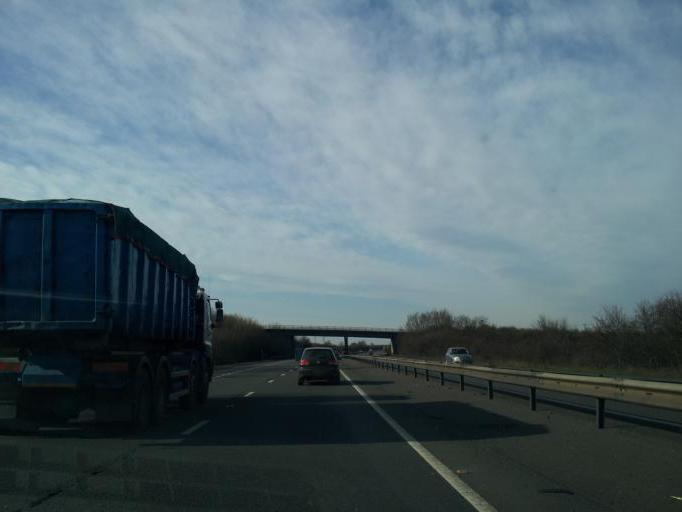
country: GB
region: England
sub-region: Lincolnshire
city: Long Bennington
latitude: 52.9804
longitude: -0.7481
